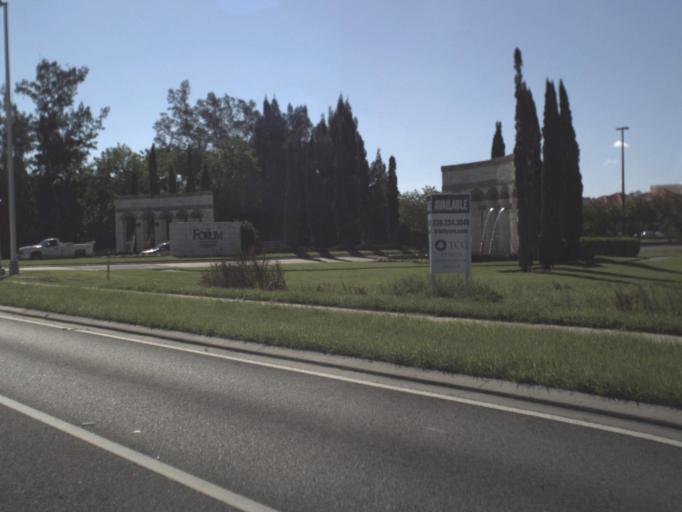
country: US
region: Florida
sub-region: Lee County
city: Tice
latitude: 26.6319
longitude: -81.7930
